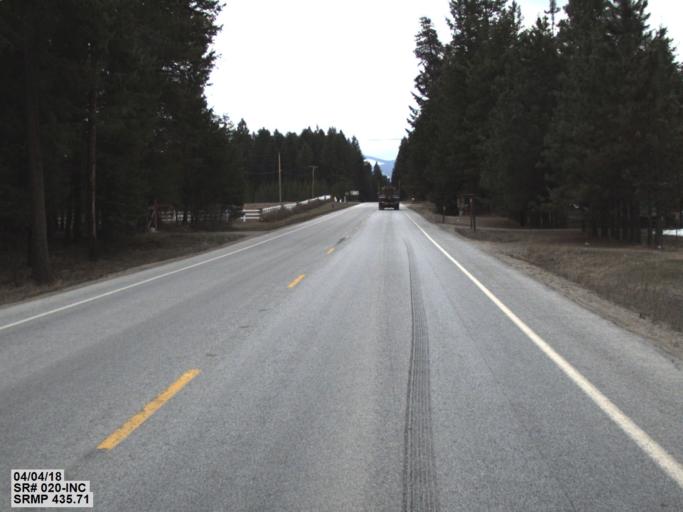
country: US
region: Washington
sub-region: Pend Oreille County
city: Newport
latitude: 48.1974
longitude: -117.0583
